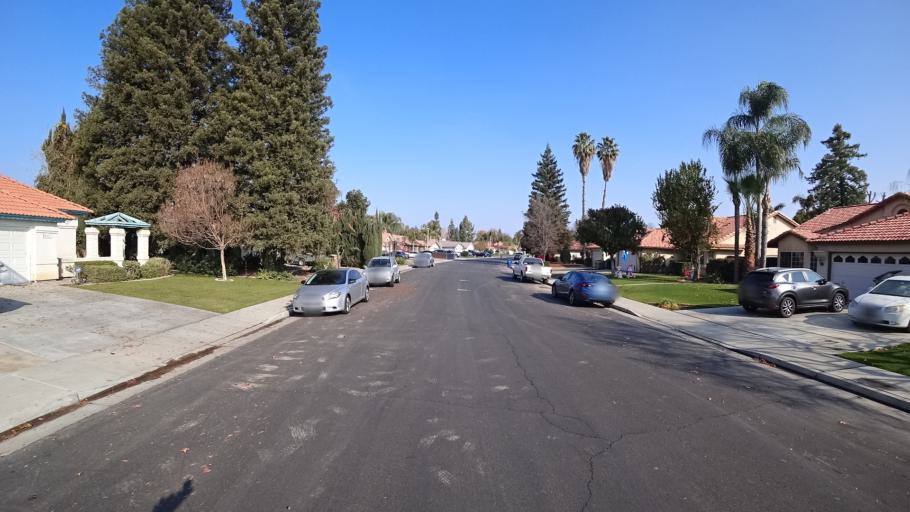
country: US
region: California
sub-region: Kern County
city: Greenacres
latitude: 35.3065
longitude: -119.0875
